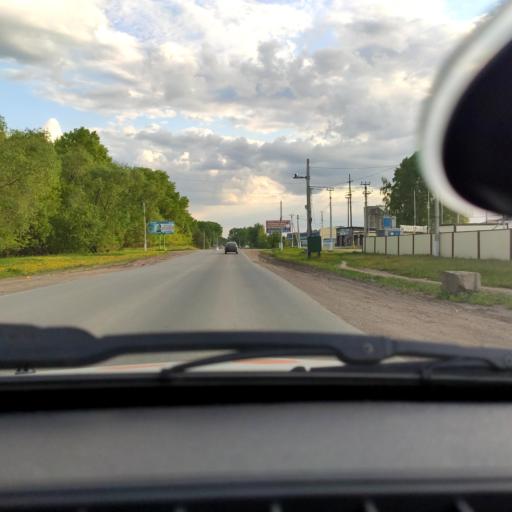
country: RU
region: Bashkortostan
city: Blagoveshchensk
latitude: 55.0458
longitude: 56.0074
